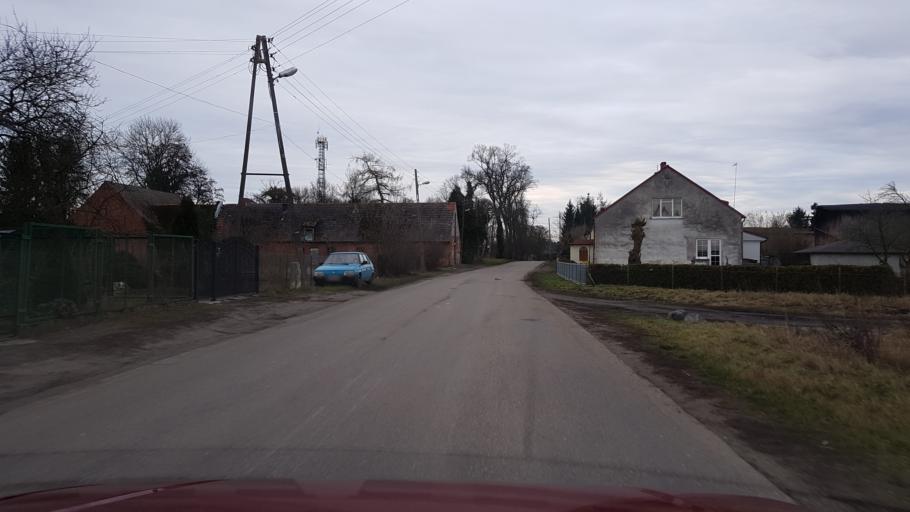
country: PL
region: West Pomeranian Voivodeship
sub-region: Powiat policki
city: Dobra
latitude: 53.5477
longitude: 14.4614
